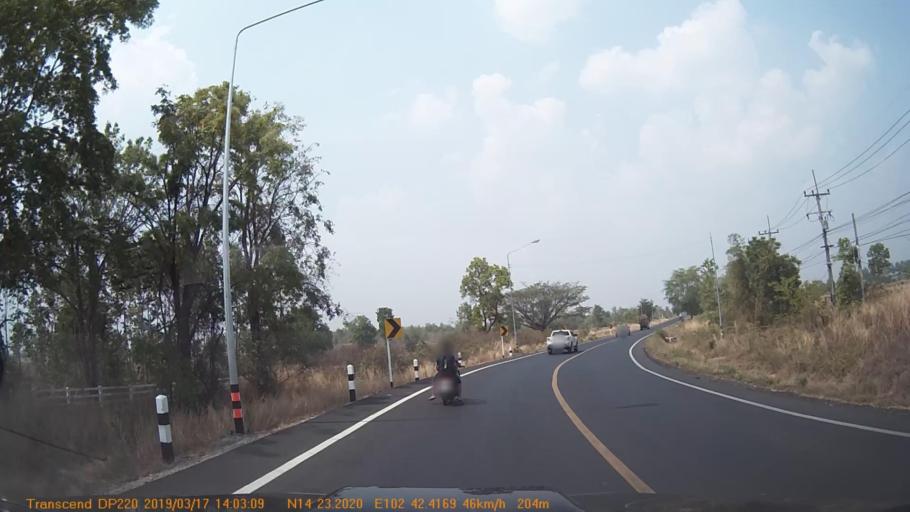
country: TH
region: Buriram
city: Pa Kham
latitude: 14.3868
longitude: 102.7070
